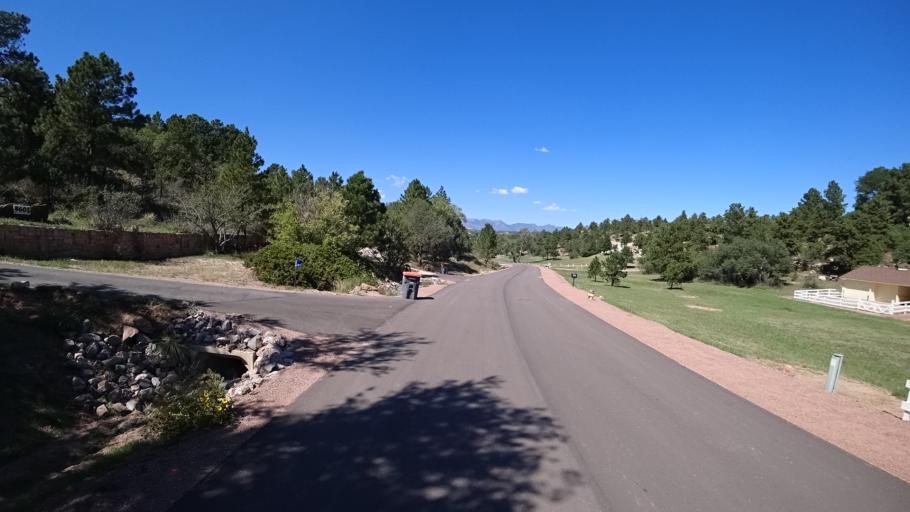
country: US
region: Colorado
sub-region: El Paso County
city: Cimarron Hills
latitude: 38.8607
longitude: -104.7420
